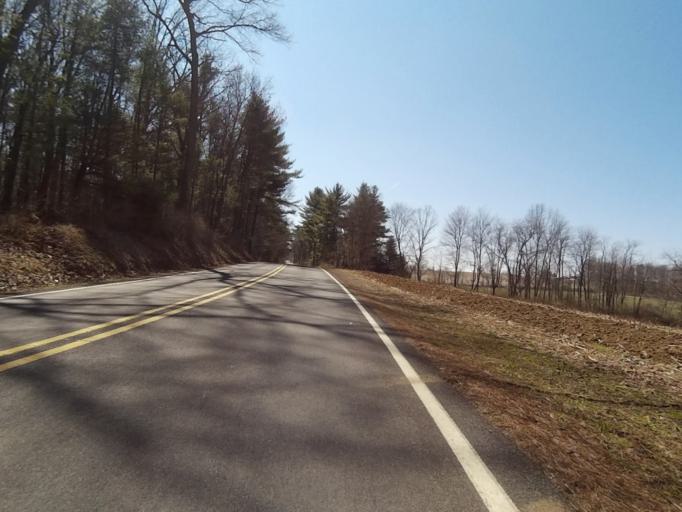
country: US
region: Pennsylvania
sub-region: Centre County
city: Stormstown
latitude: 40.7535
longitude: -77.9890
